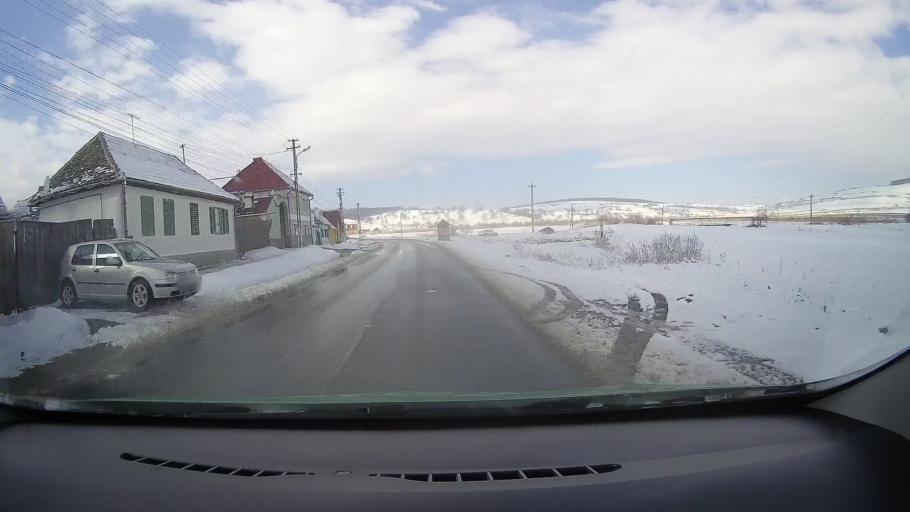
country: RO
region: Sibiu
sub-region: Comuna Altina
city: Altina
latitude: 45.9370
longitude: 24.4600
